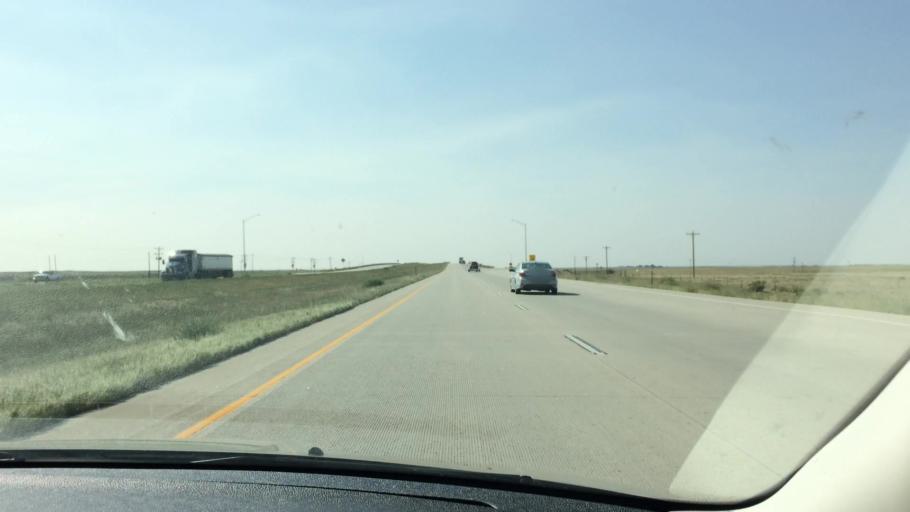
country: US
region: Colorado
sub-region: Arapahoe County
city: Byers
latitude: 39.6792
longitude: -104.1105
